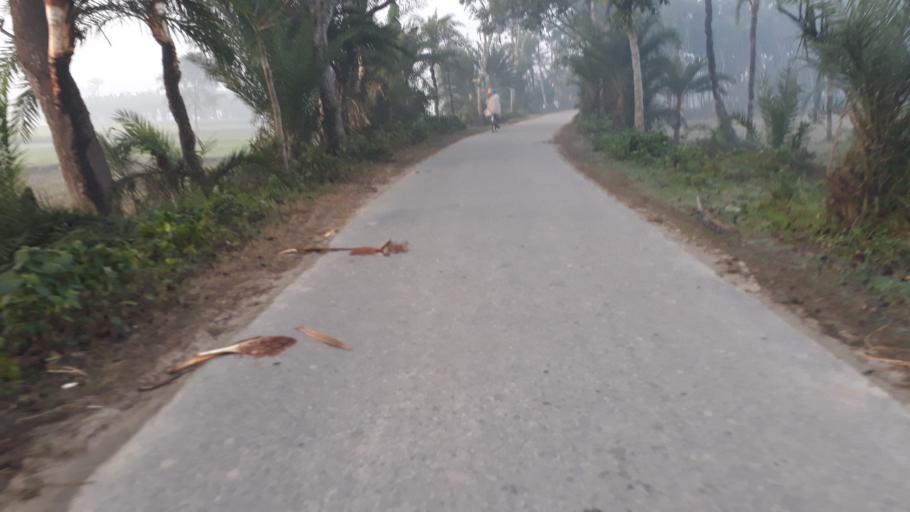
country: BD
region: Khulna
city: Jhingergacha
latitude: 23.2630
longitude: 88.9342
